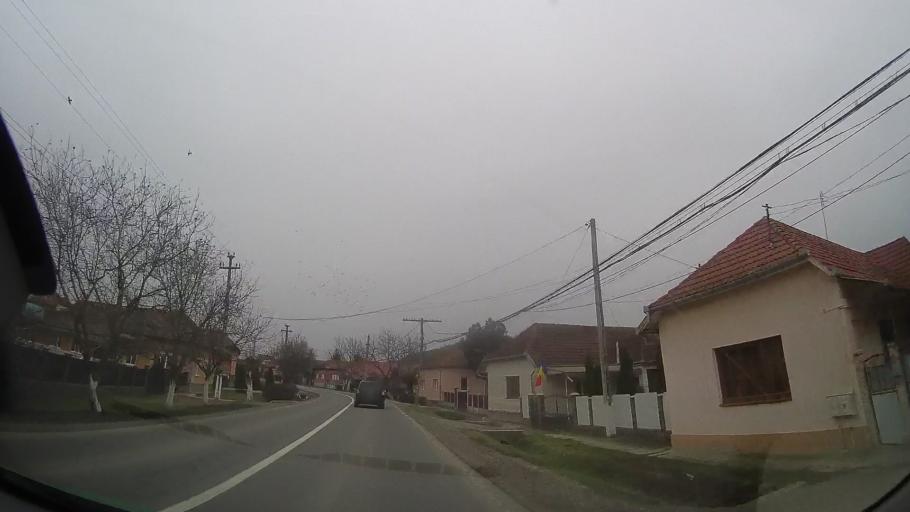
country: RO
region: Mures
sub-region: Comuna Ceausu de Campie
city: Ceausu de Campie
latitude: 46.6141
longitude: 24.5271
